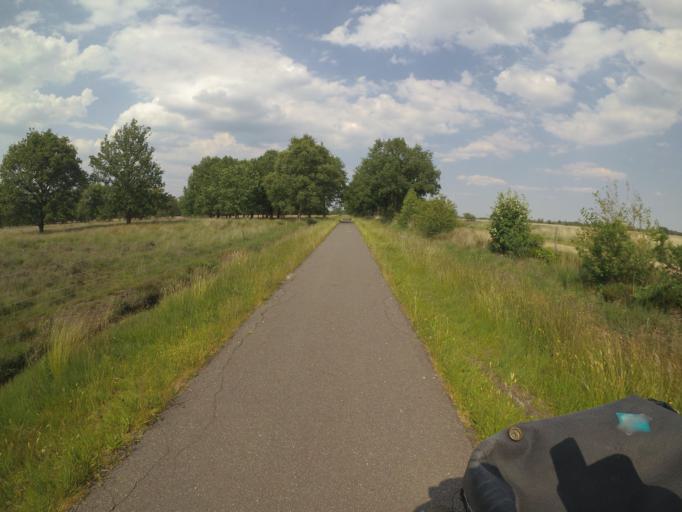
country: NL
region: Drenthe
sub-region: Gemeente Assen
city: Assen
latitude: 52.9629
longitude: 6.4982
